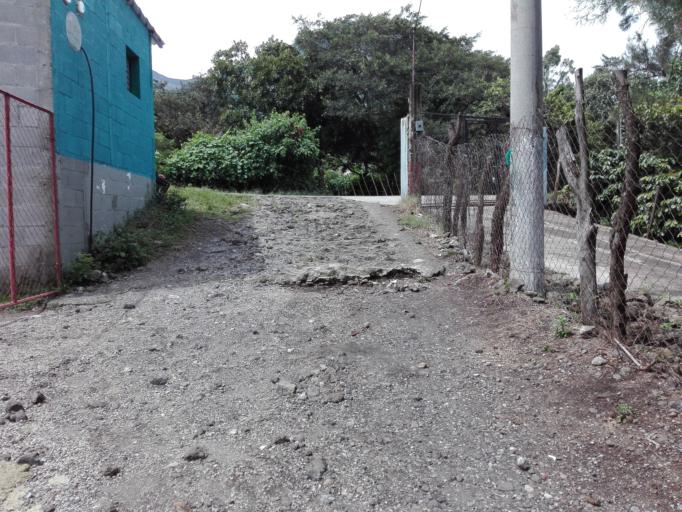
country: GT
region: Escuintla
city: San Vicente Pacaya
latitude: 14.3631
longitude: -90.5680
